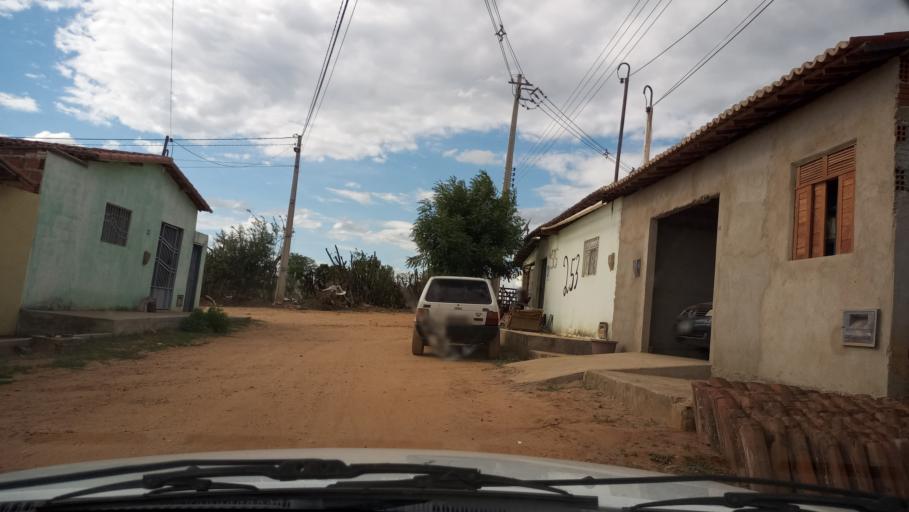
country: BR
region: Rio Grande do Norte
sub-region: Sao Tome
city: Sao Tome
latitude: -5.9415
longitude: -35.9262
